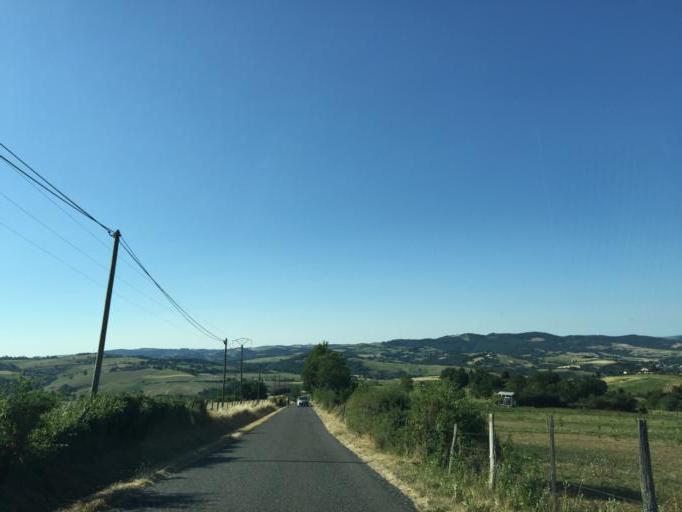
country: FR
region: Rhone-Alpes
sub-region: Departement de la Loire
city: Saint-Jean-Bonnefonds
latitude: 45.4472
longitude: 4.4905
